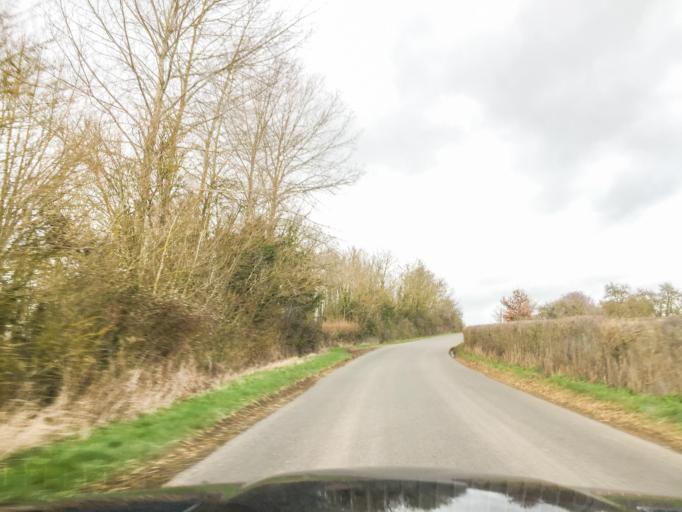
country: GB
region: England
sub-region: Warwickshire
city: Shipston on Stour
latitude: 52.0859
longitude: -1.6013
